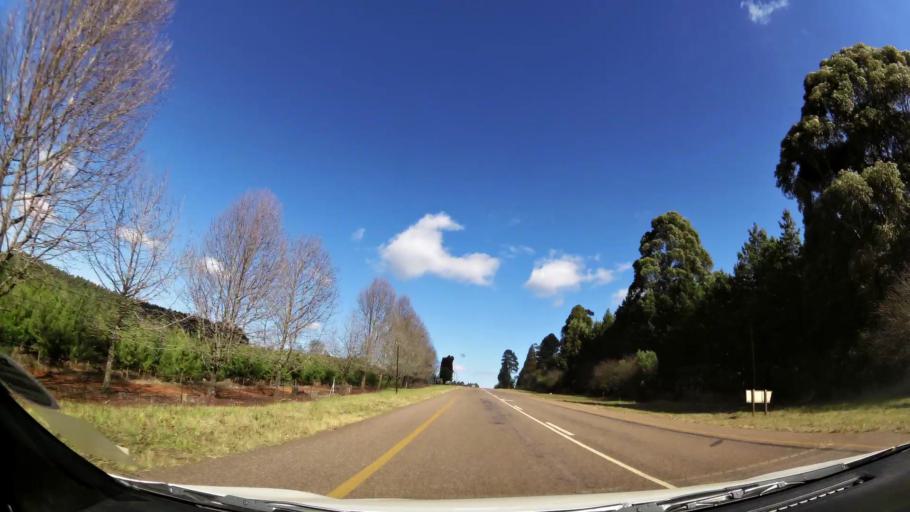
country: ZA
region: Limpopo
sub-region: Capricorn District Municipality
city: Mankoeng
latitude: -23.8969
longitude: 29.9937
